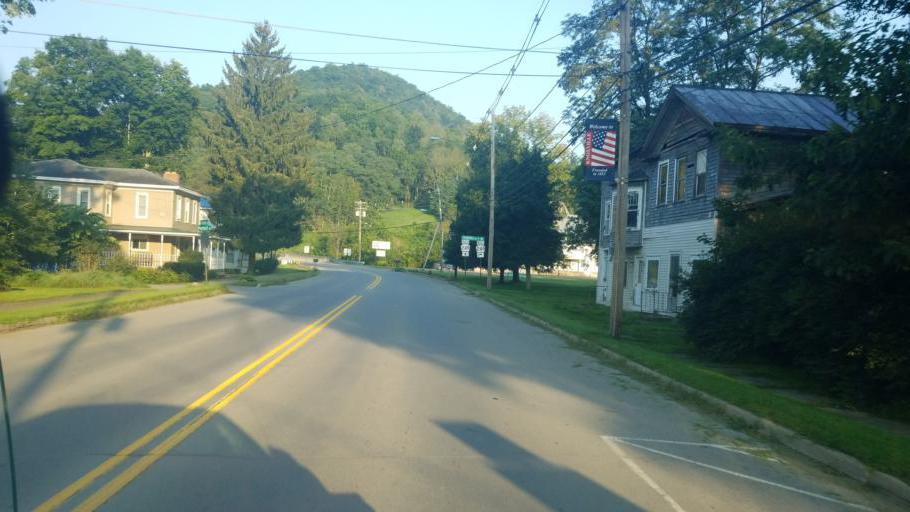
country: US
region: Pennsylvania
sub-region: Tioga County
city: Westfield
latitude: 41.9577
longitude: -77.4422
